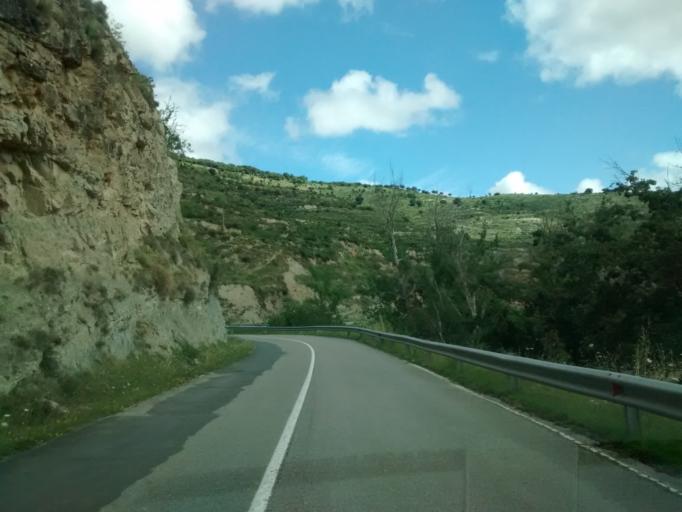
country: ES
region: La Rioja
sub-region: Provincia de La Rioja
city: Terroba
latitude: 42.2543
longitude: -2.4546
